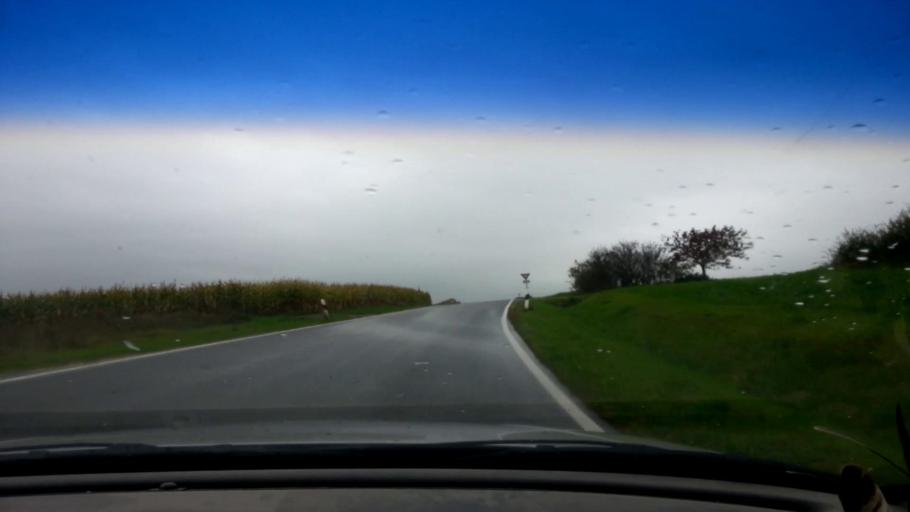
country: DE
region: Bavaria
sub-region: Upper Franconia
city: Poxdorf
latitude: 49.8754
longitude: 11.0979
